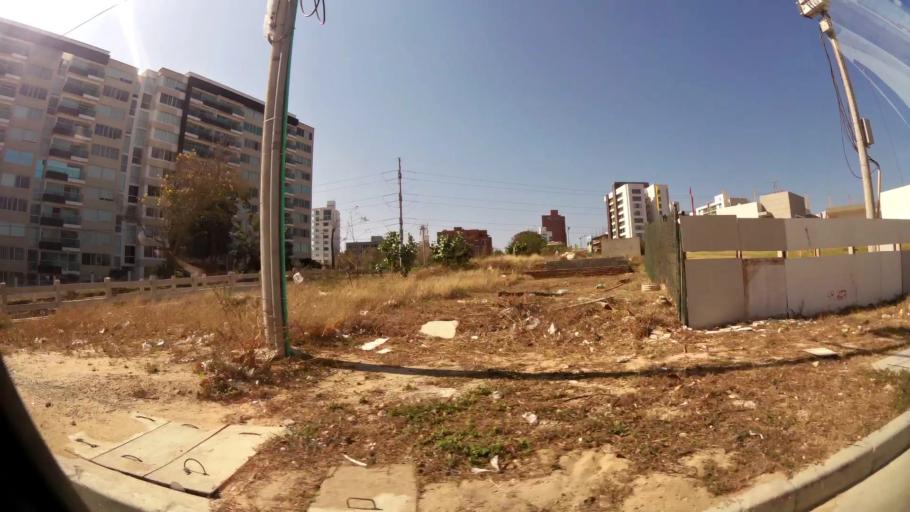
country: CO
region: Atlantico
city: Barranquilla
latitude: 11.0207
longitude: -74.8196
